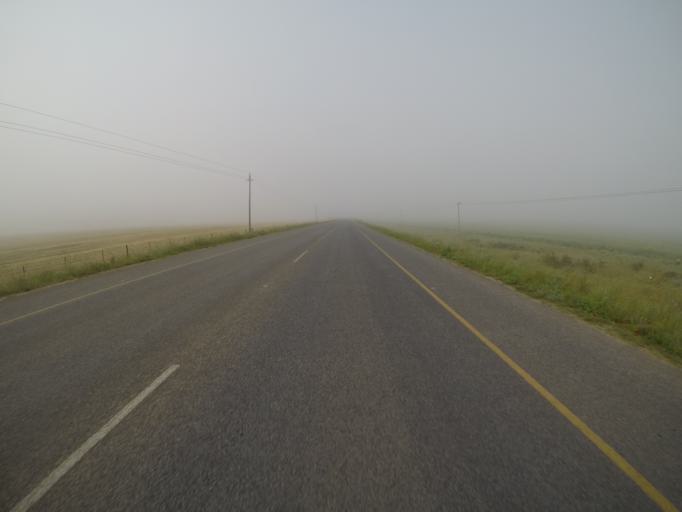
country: ZA
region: Western Cape
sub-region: City of Cape Town
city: Kraaifontein
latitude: -33.6757
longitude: 18.7067
